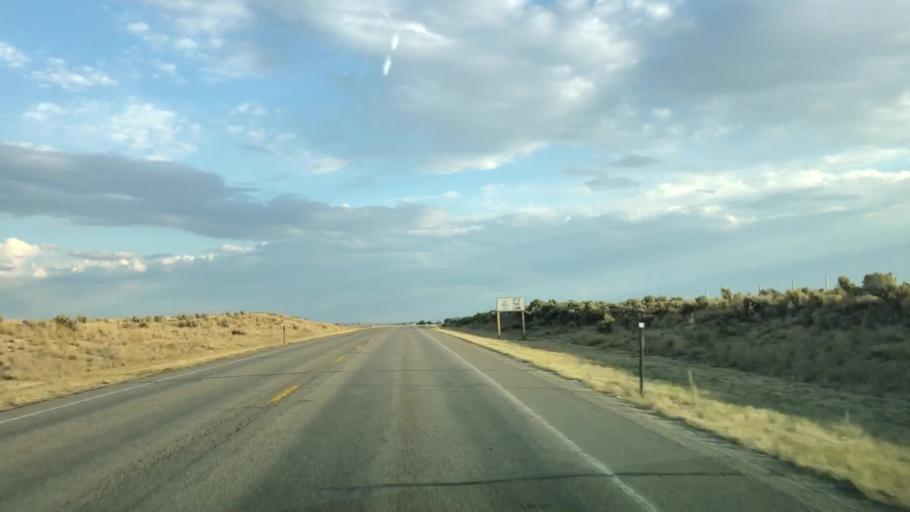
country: US
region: Wyoming
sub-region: Sweetwater County
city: North Rock Springs
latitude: 42.0975
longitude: -109.4445
